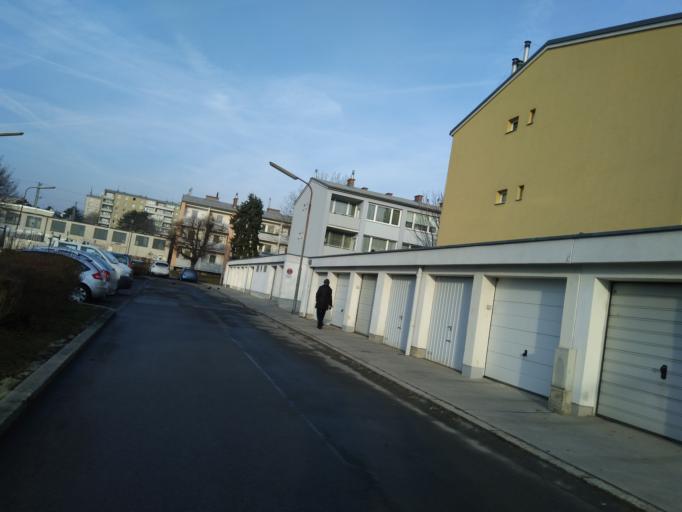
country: AT
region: Lower Austria
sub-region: Politischer Bezirk Modling
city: Perchtoldsdorf
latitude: 48.1443
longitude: 16.2894
